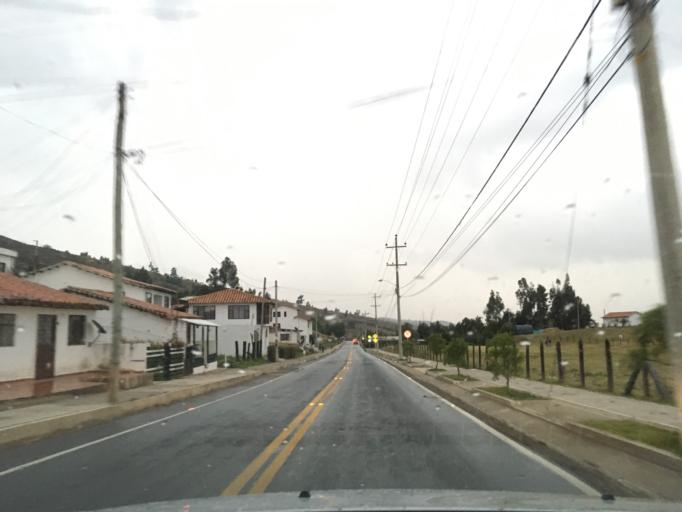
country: CO
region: Cundinamarca
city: Guatavita
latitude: 4.9322
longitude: -73.8331
